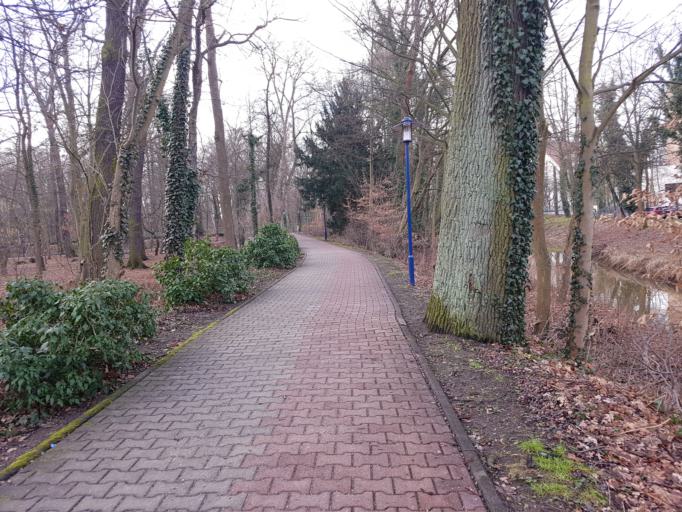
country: DE
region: Brandenburg
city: Bad Liebenwerda
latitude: 51.5164
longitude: 13.4009
